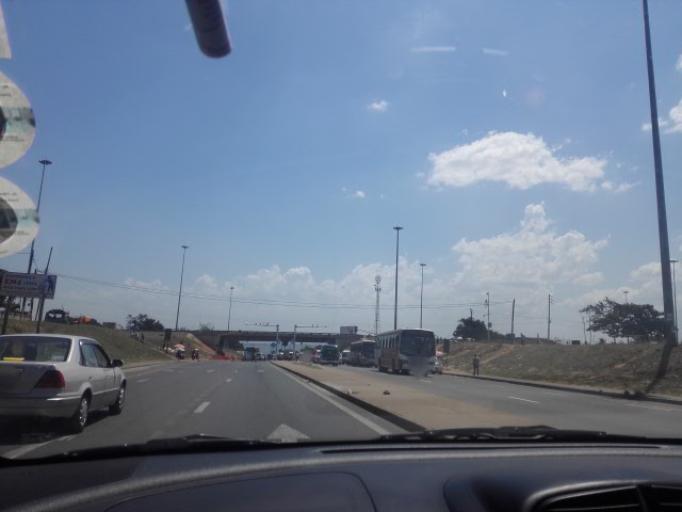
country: MZ
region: Maputo City
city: Maputo
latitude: -25.9429
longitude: 32.5425
